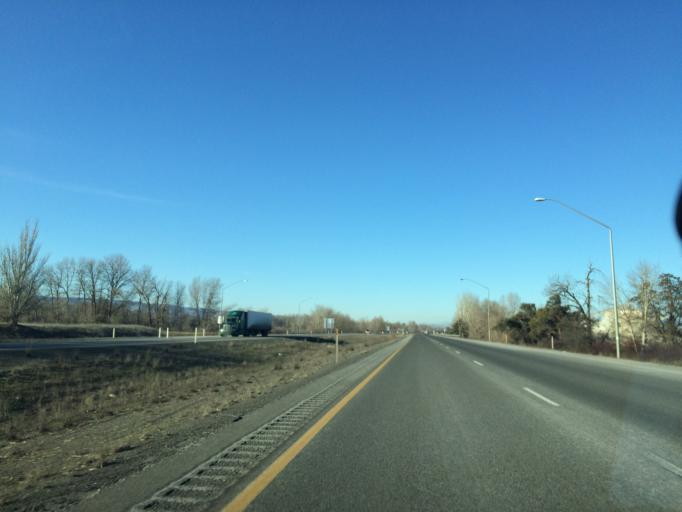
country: US
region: Washington
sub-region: Kittitas County
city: Ellensburg
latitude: 47.0098
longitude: -120.5965
